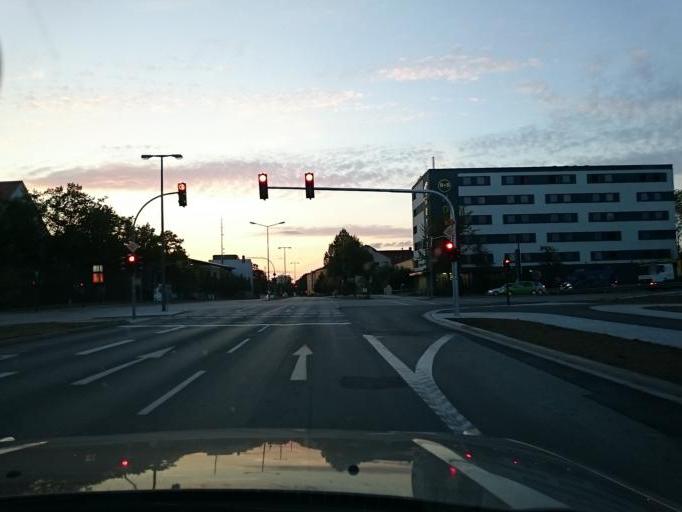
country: DE
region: Bavaria
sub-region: Upper Palatinate
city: Regensburg
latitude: 49.0011
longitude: 12.1276
